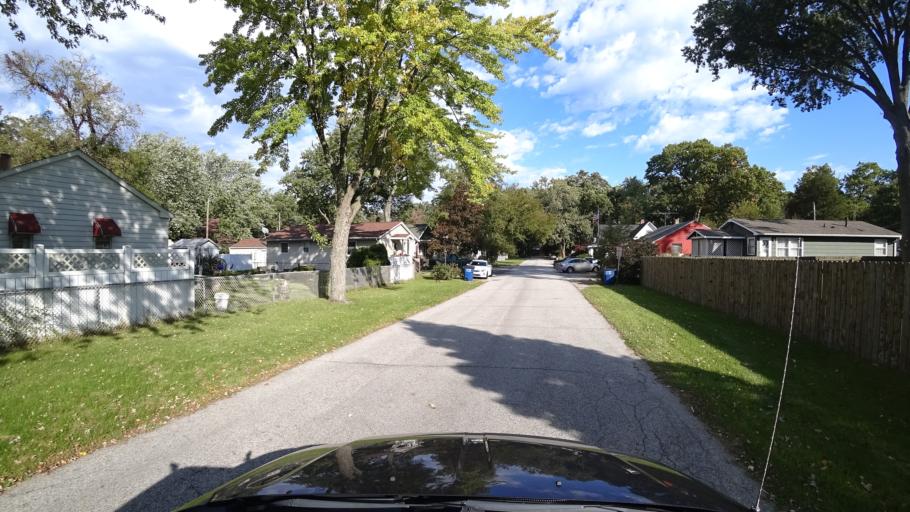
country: US
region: Indiana
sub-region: LaPorte County
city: Trail Creek
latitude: 41.7022
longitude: -86.8735
